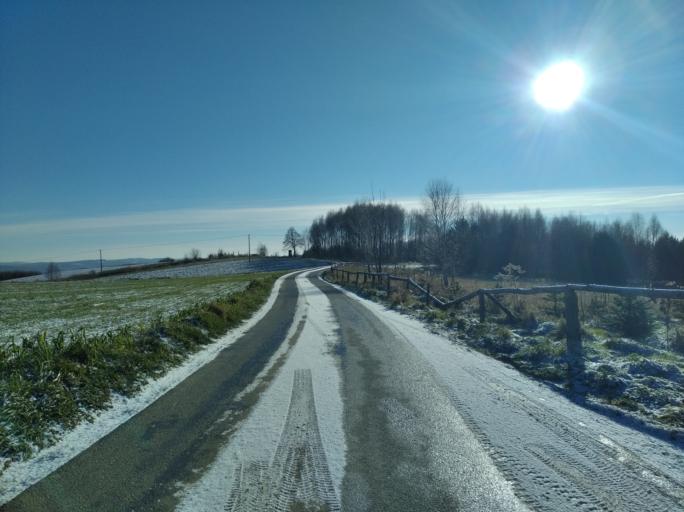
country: PL
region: Subcarpathian Voivodeship
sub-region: Powiat ropczycko-sedziszowski
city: Iwierzyce
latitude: 49.9667
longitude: 21.7493
